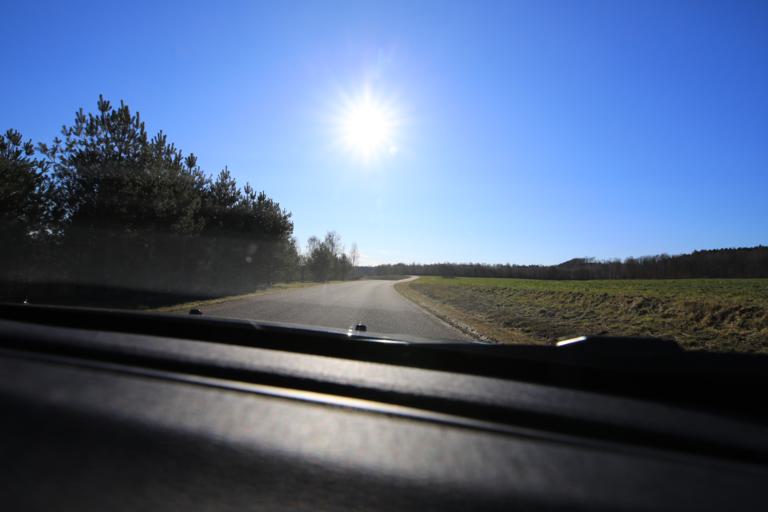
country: SE
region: Halland
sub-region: Varbergs Kommun
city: Tvaaker
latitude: 57.0673
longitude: 12.4667
